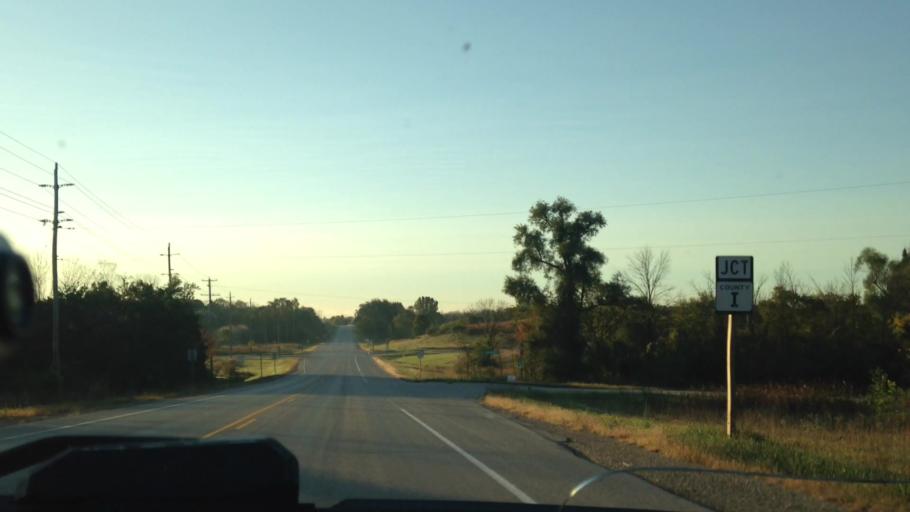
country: US
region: Wisconsin
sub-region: Ozaukee County
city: Saukville
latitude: 43.3972
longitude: -87.9817
